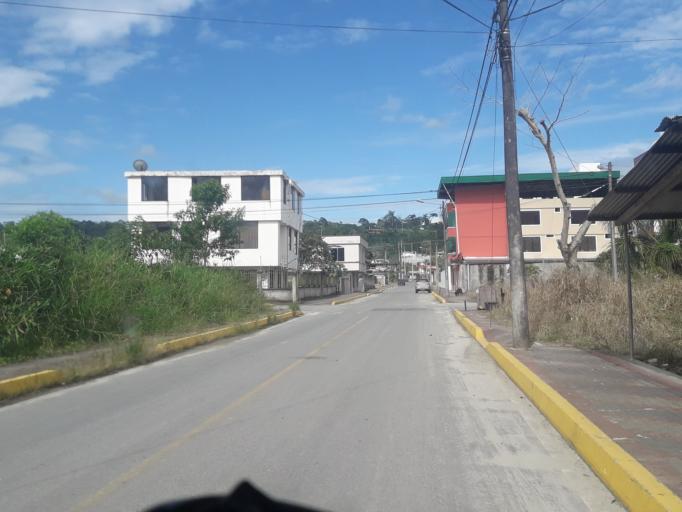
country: EC
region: Napo
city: Tena
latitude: -1.0079
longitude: -77.8154
